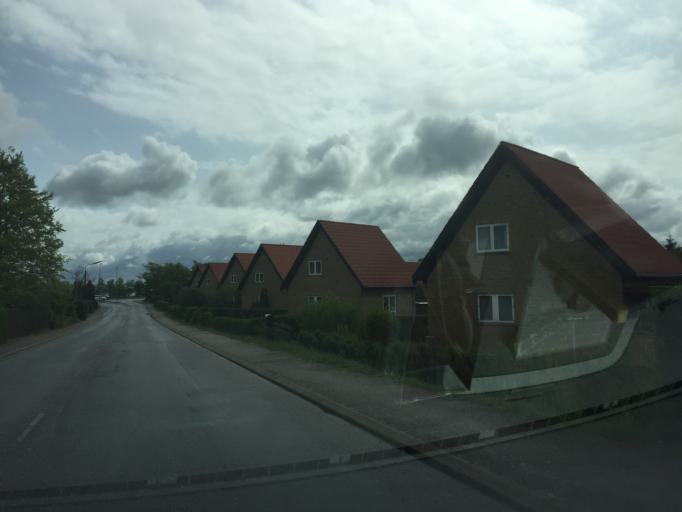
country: DK
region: Capital Region
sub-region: Halsnaes Kommune
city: Frederiksvaerk
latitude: 55.9484
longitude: 12.0428
